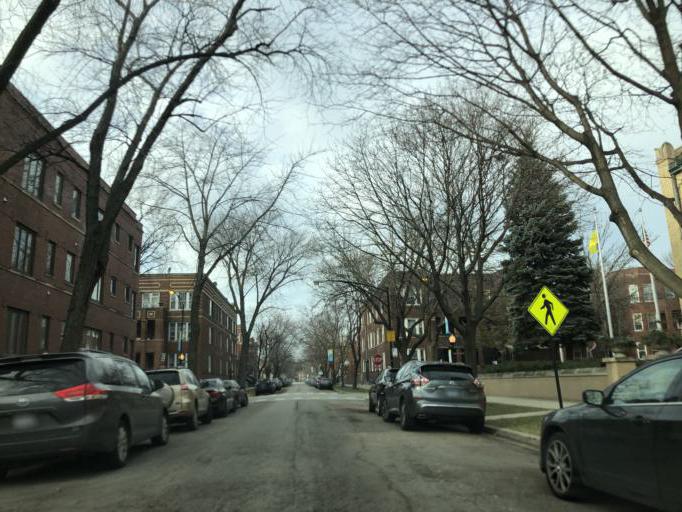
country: US
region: Illinois
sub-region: Cook County
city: Chicago
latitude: 41.8968
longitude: -87.6838
